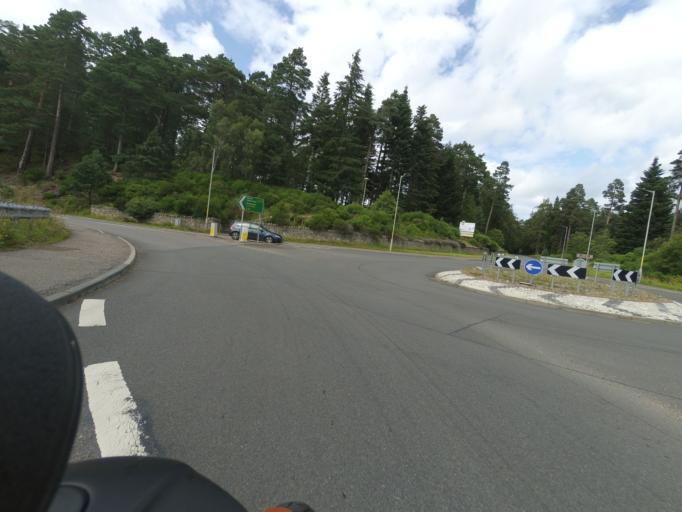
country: GB
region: Scotland
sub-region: Highland
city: Grantown on Spey
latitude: 57.3221
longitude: -3.6062
